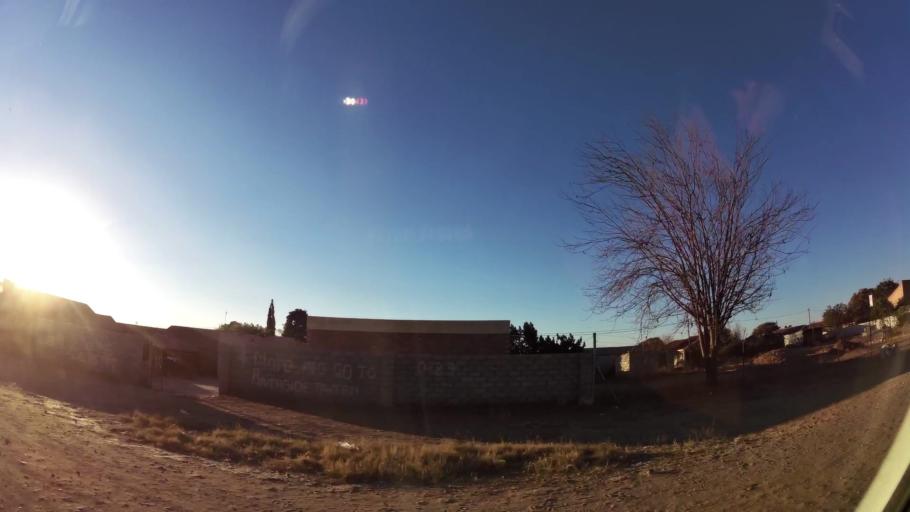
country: ZA
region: Limpopo
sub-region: Capricorn District Municipality
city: Polokwane
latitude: -23.8539
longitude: 29.3635
